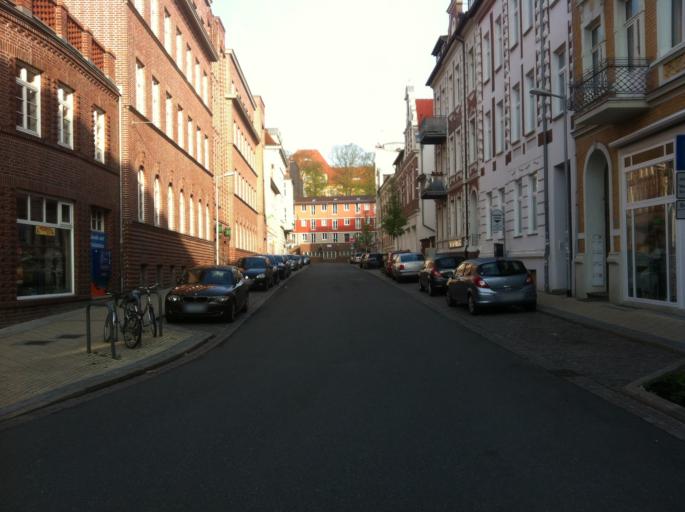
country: DE
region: Mecklenburg-Vorpommern
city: Schwerin
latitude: 53.6267
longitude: 11.4121
